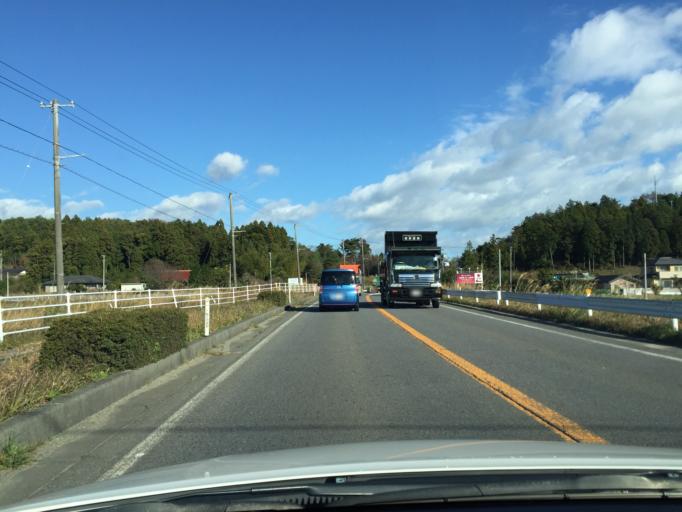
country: JP
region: Fukushima
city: Namie
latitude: 37.3042
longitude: 140.9942
